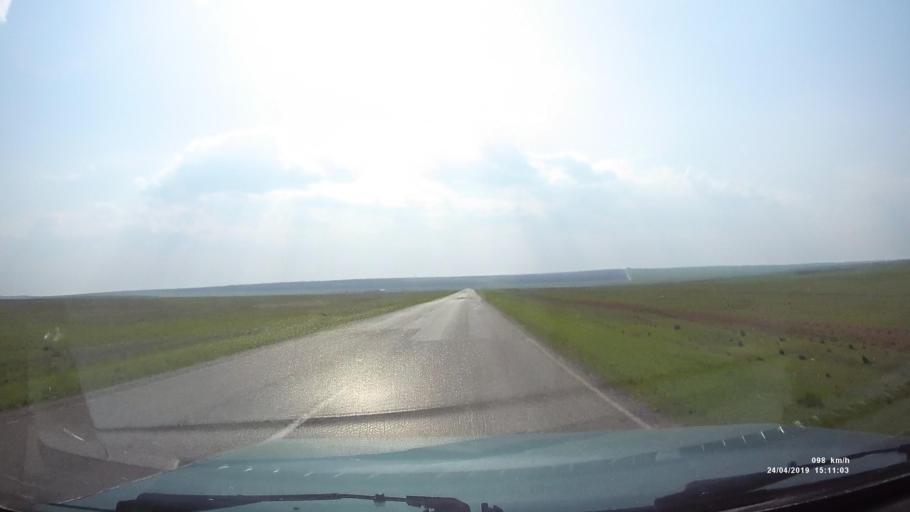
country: RU
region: Rostov
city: Remontnoye
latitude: 46.5460
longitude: 43.3287
